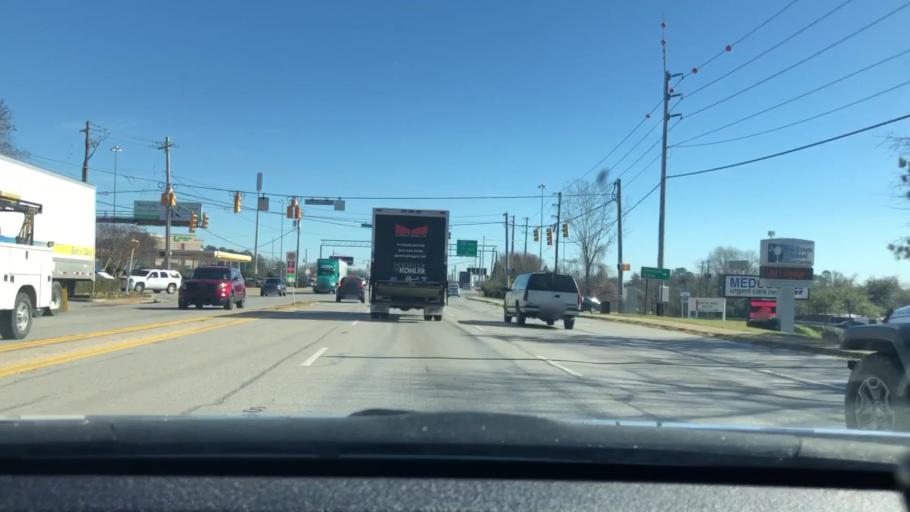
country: US
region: South Carolina
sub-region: Lexington County
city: Oak Grove
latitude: 34.0042
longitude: -81.1134
